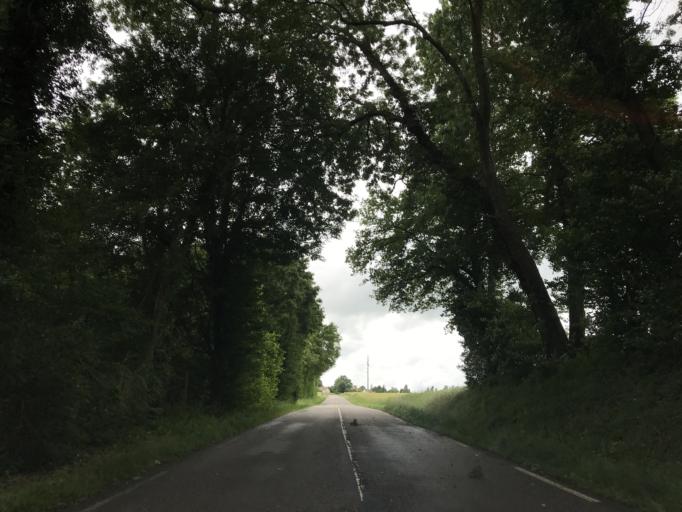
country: FR
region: Ile-de-France
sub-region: Departement des Yvelines
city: Rosny-sur-Seine
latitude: 48.9799
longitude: 1.6022
